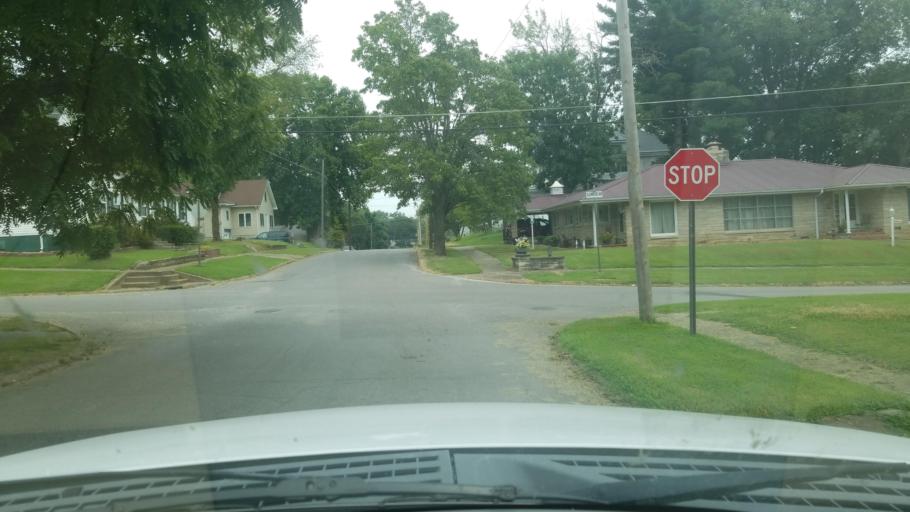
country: US
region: Illinois
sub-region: Saline County
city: Eldorado
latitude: 37.8176
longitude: -88.4433
